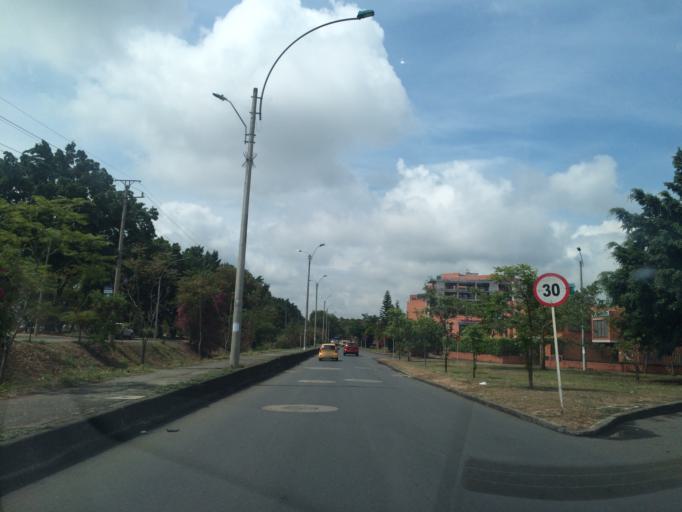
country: CO
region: Valle del Cauca
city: Cali
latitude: 3.3766
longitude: -76.5254
